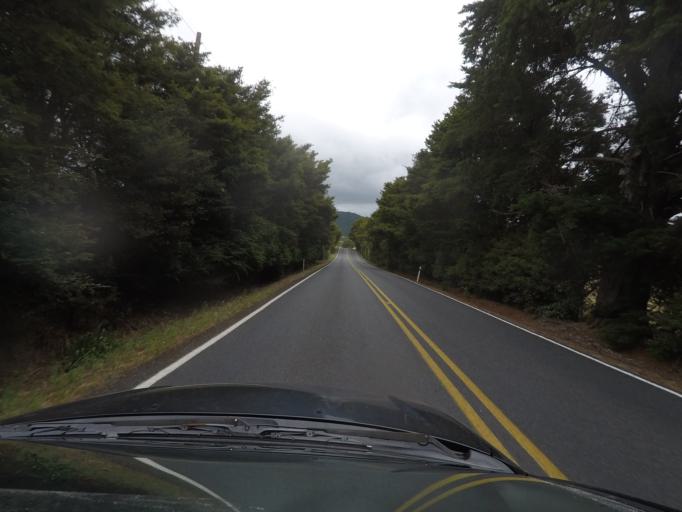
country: NZ
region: Auckland
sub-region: Auckland
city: Wellsford
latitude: -36.2872
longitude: 174.6307
